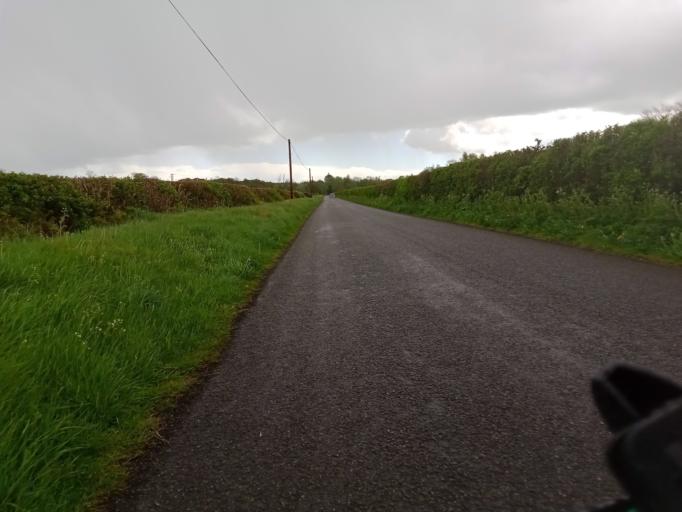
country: IE
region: Leinster
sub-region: Kilkenny
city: Kilkenny
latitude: 52.6785
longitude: -7.2638
